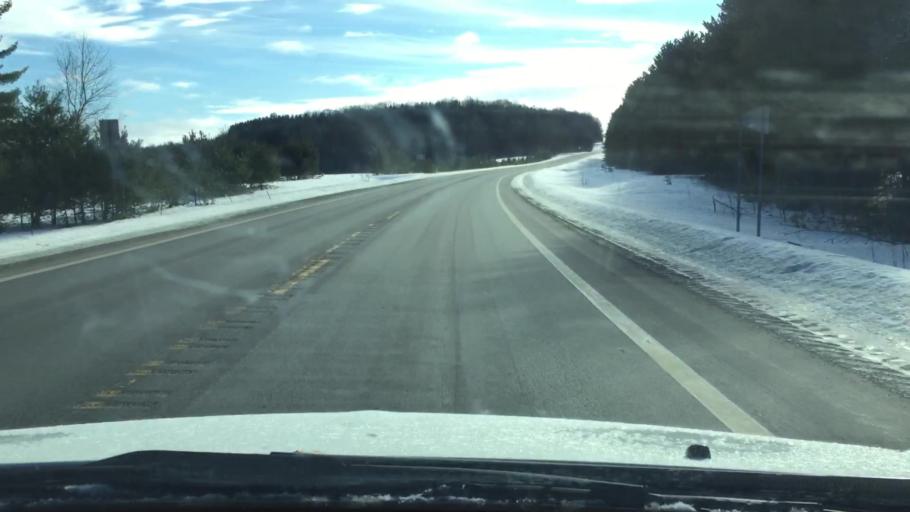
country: US
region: Michigan
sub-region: Antrim County
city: Mancelona
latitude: 44.9817
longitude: -85.0537
